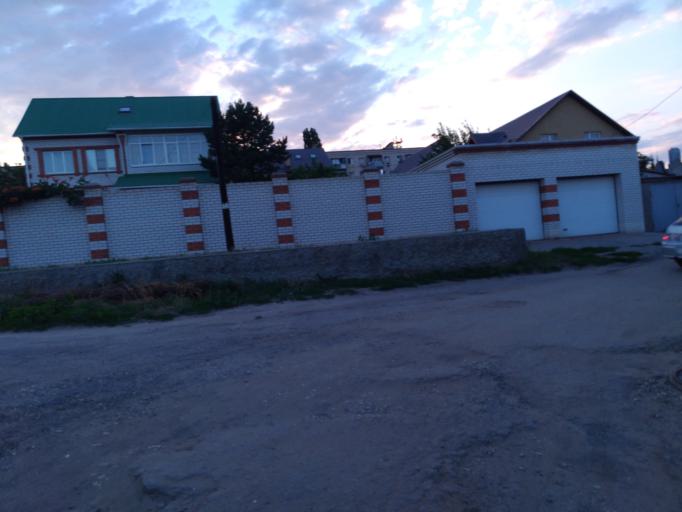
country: RU
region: Volgograd
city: Volgograd
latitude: 48.6705
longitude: 44.4506
